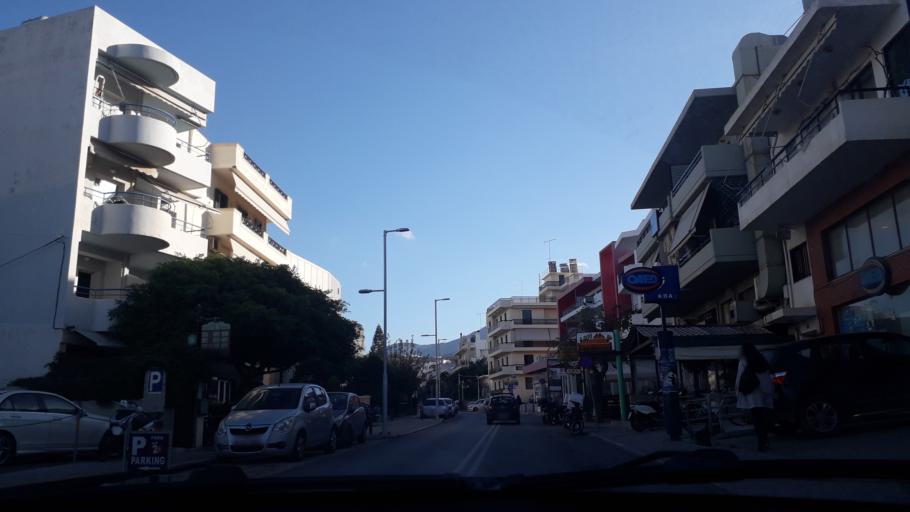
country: GR
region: Crete
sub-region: Nomos Rethymnis
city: Rethymno
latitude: 35.3655
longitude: 24.4704
